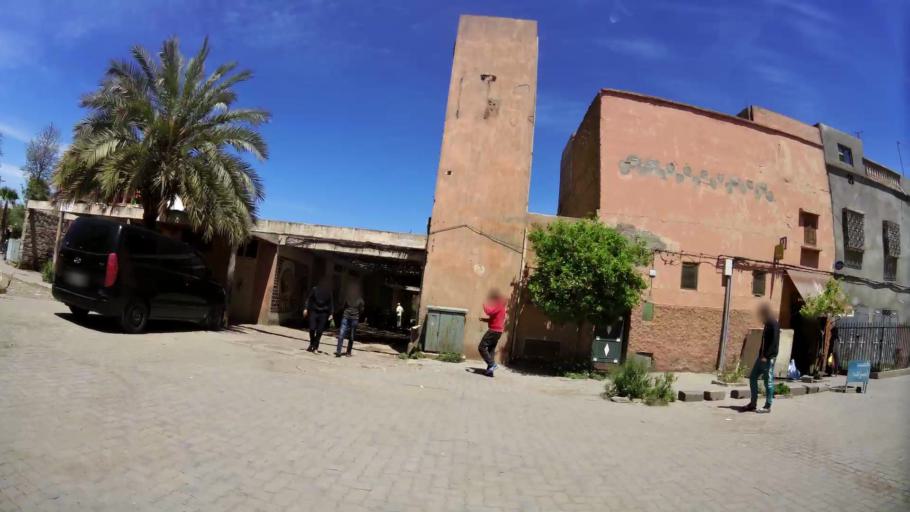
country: MA
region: Marrakech-Tensift-Al Haouz
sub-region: Marrakech
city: Marrakesh
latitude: 31.6294
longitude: -8.0448
